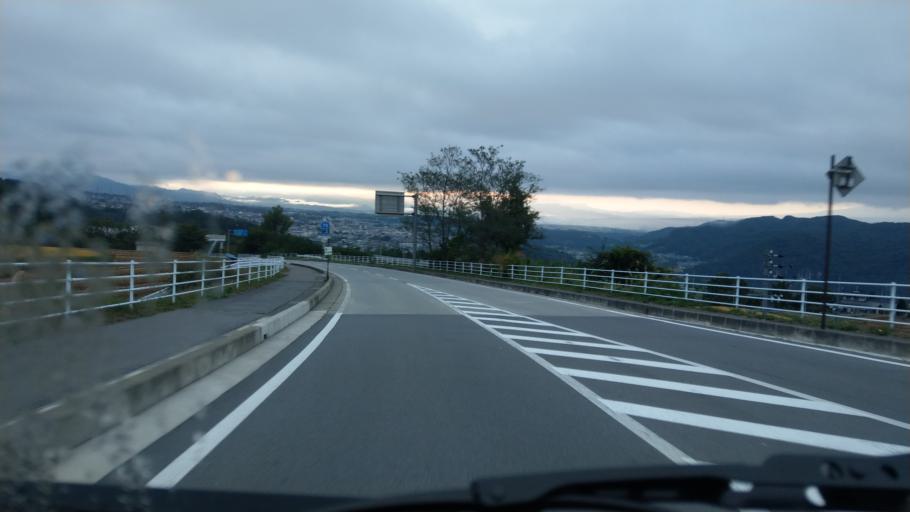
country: JP
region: Nagano
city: Komoro
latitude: 36.3502
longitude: 138.4047
